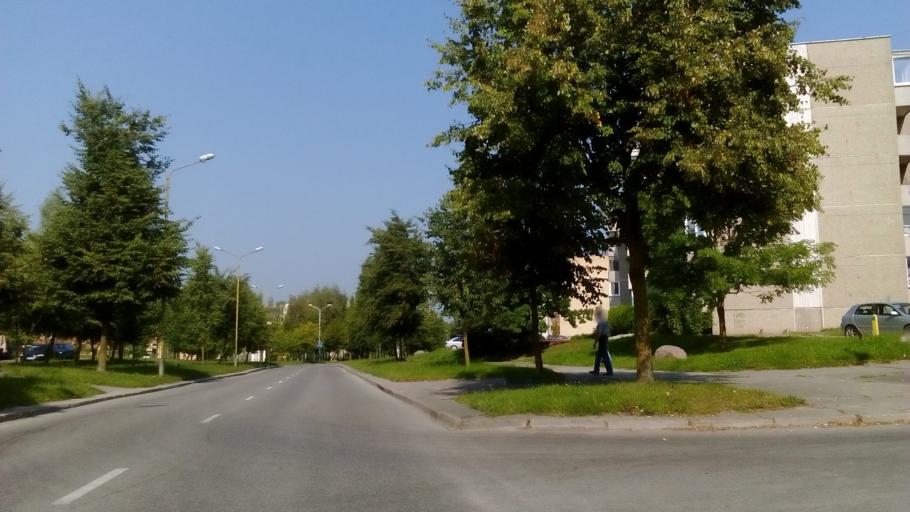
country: LT
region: Alytaus apskritis
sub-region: Alytus
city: Alytus
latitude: 54.3970
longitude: 24.0198
